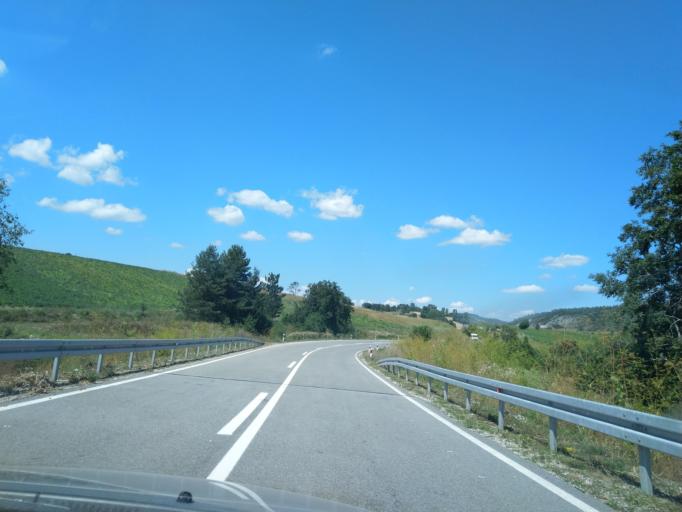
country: RS
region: Central Serbia
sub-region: Zlatiborski Okrug
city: Sjenica
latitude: 43.3246
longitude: 19.8948
